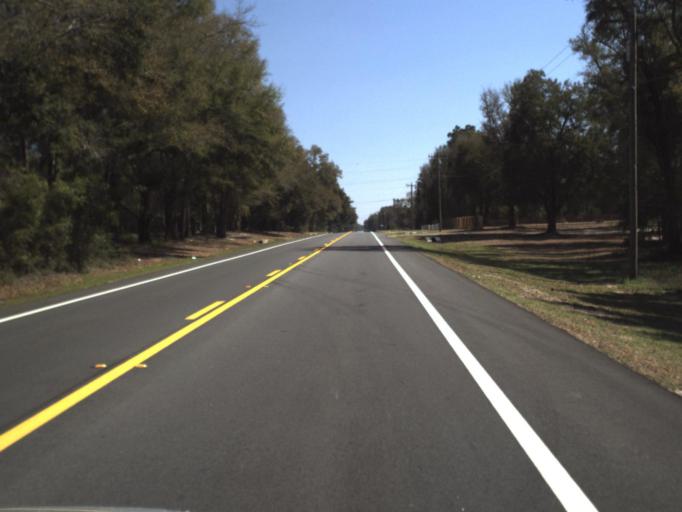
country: US
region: Florida
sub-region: Jackson County
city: Malone
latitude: 30.8670
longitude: -85.1240
